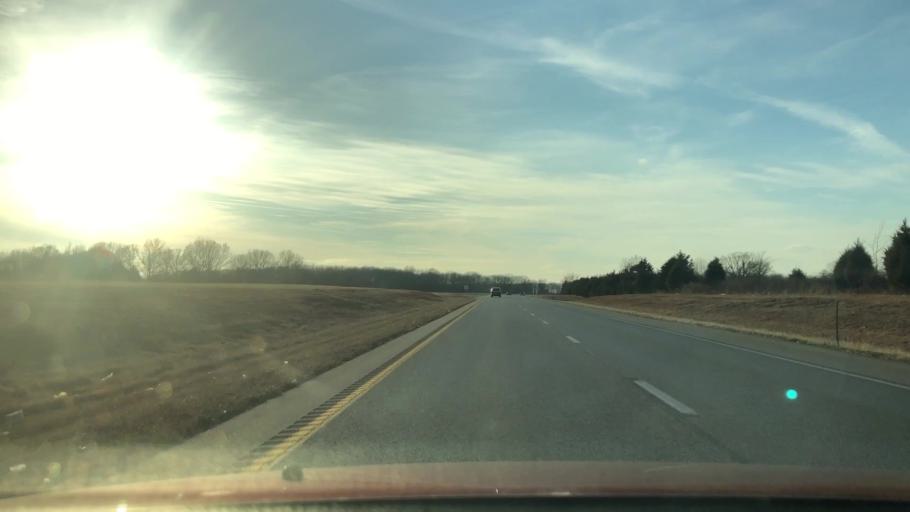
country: US
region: Missouri
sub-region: Webster County
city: Seymour
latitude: 37.1309
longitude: -92.7271
